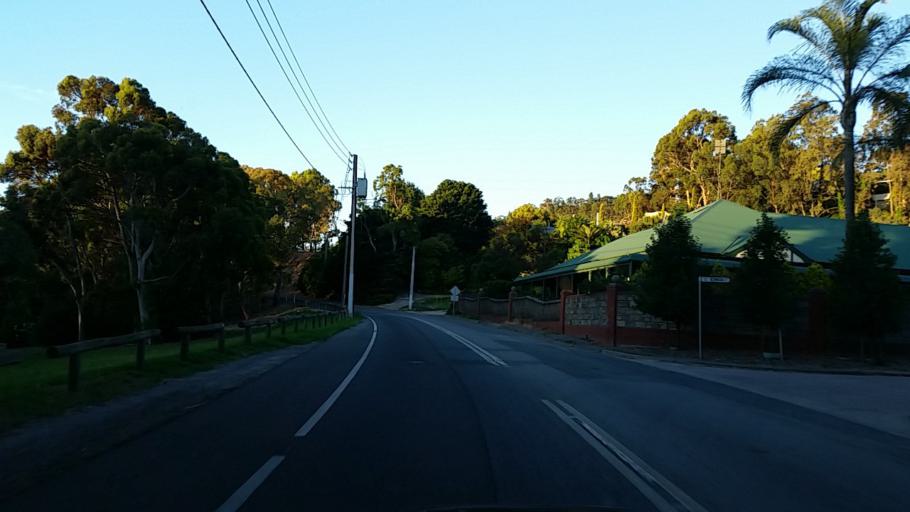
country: AU
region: South Australia
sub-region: Campbelltown
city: Athelstone
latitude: -34.8625
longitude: 138.7212
